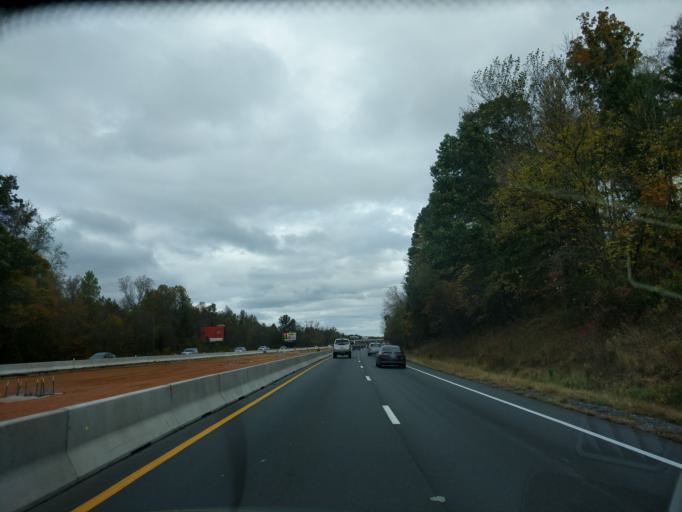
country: US
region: North Carolina
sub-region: Rowan County
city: China Grove
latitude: 35.5349
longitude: -80.5737
